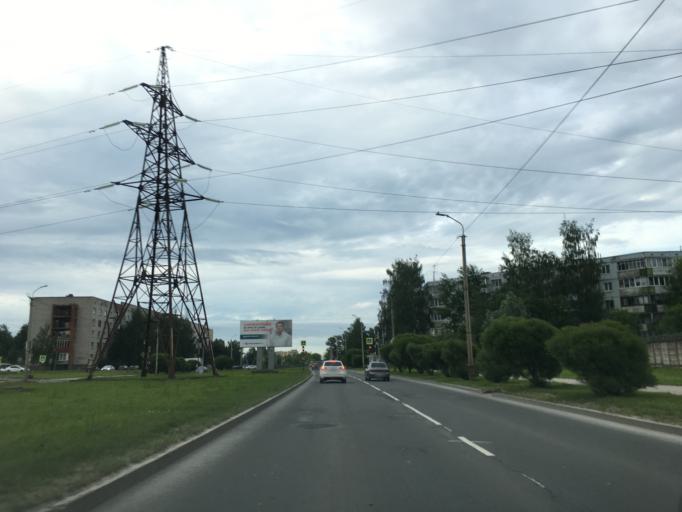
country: RU
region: Pskov
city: Pskov
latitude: 57.8366
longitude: 28.3011
